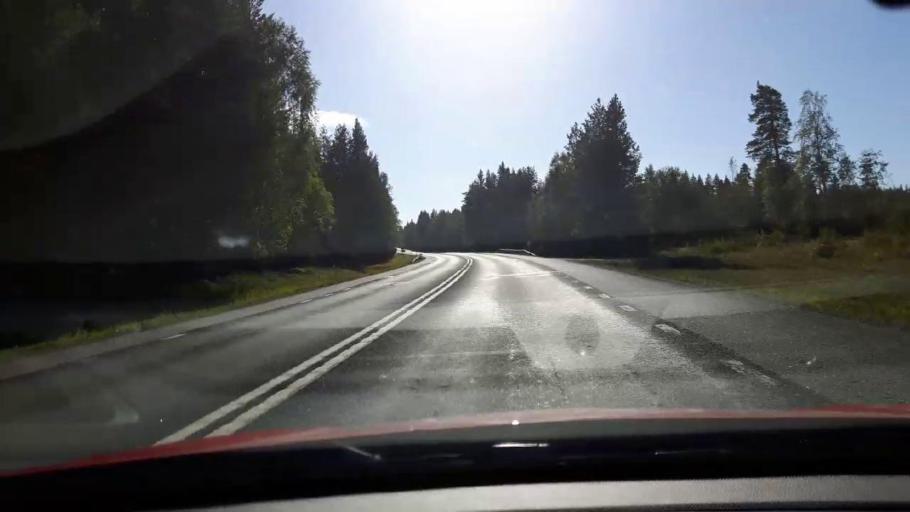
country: SE
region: Jaemtland
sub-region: Braecke Kommun
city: Braecke
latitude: 62.7160
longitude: 15.4587
